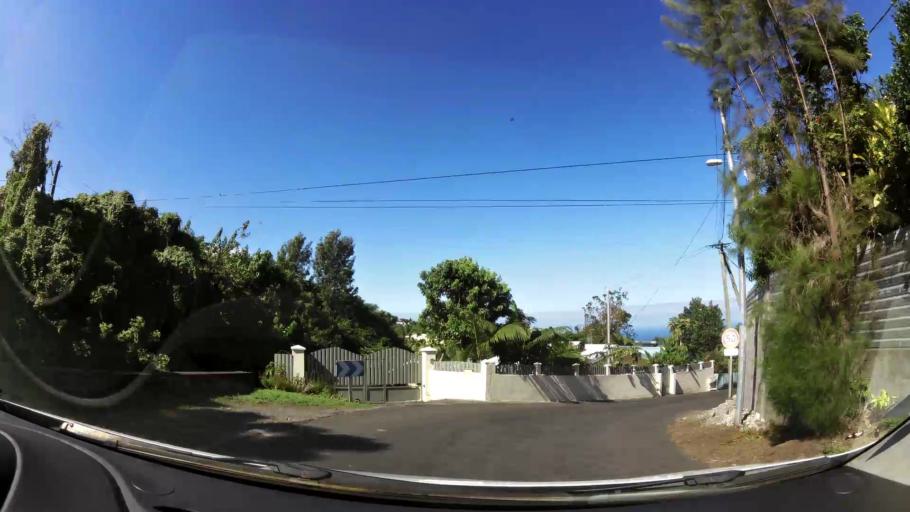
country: RE
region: Reunion
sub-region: Reunion
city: Le Tampon
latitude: -21.2644
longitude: 55.5035
